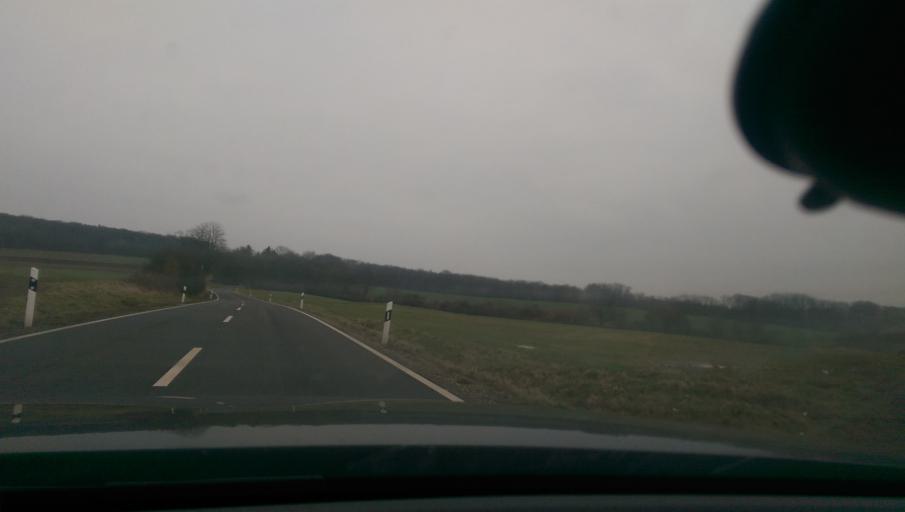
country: DE
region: Hesse
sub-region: Regierungsbezirk Kassel
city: Kaufungen
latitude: 51.3076
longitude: 9.6019
